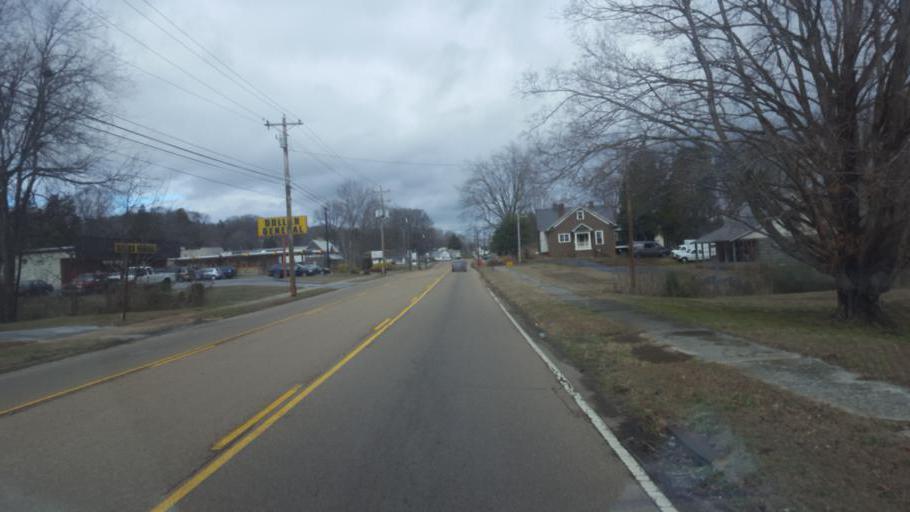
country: US
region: Tennessee
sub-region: Bradley County
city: Hopewell
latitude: 35.2833
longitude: -84.7605
